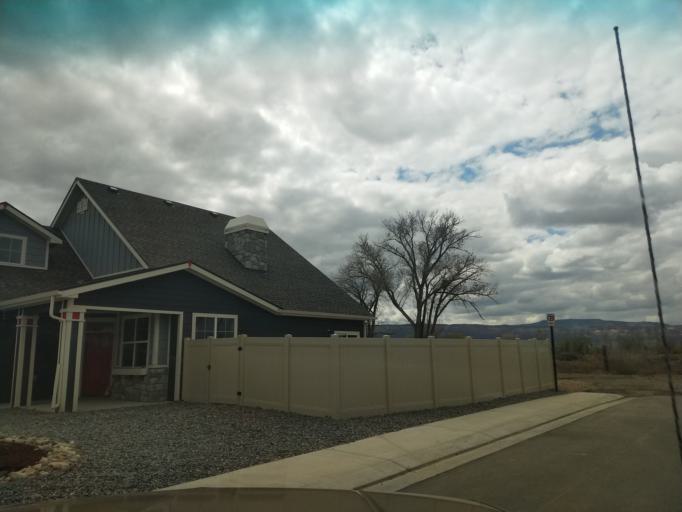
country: US
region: Colorado
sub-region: Mesa County
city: Redlands
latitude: 39.1037
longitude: -108.5937
